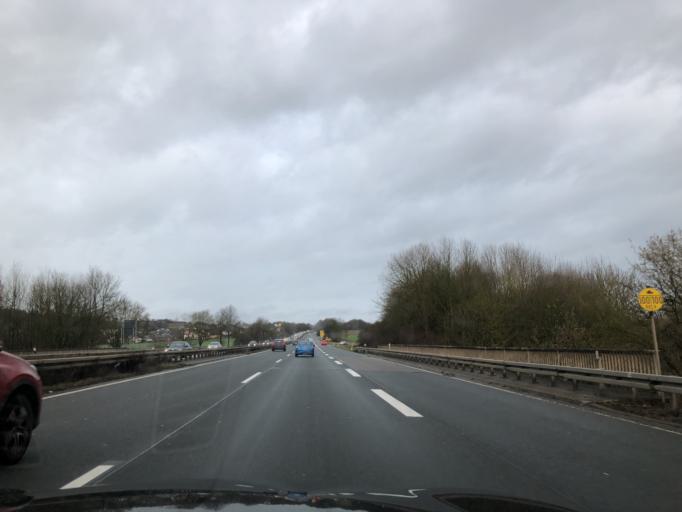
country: DE
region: Hesse
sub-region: Regierungsbezirk Giessen
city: Dehrn
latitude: 50.4287
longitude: 8.0887
